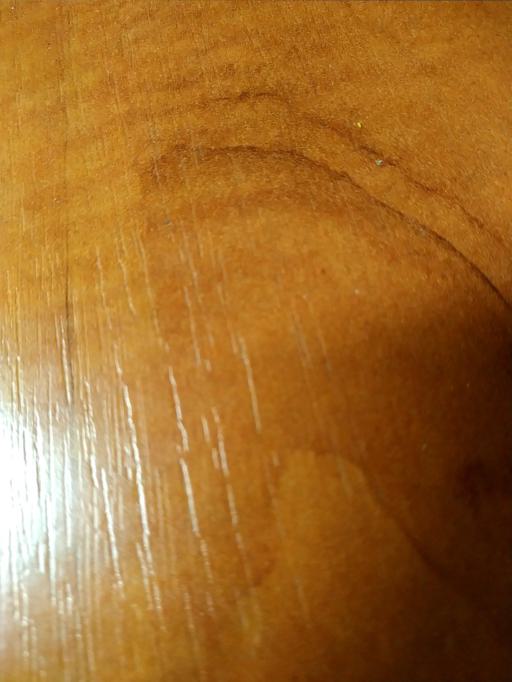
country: RU
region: Smolensk
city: Yartsevo
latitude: 55.4347
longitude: 32.7948
